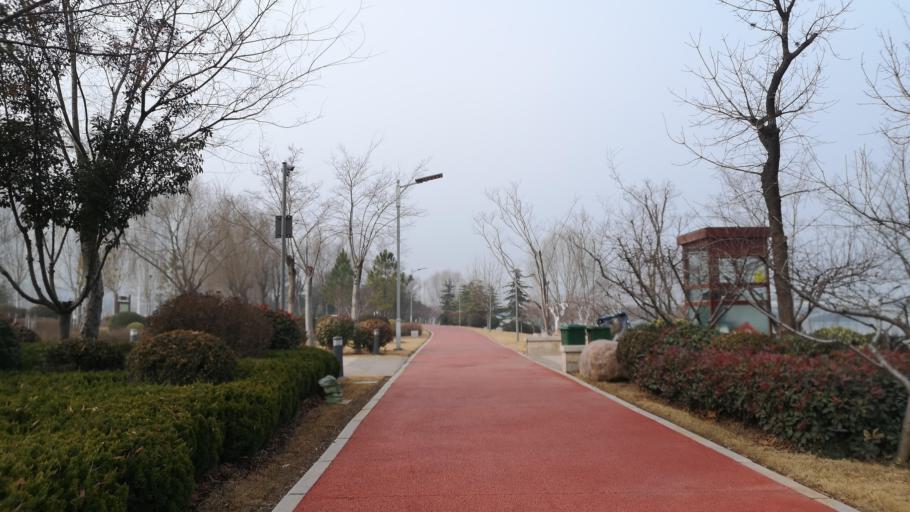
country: CN
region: Henan Sheng
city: Puyang
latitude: 35.8010
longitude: 115.0306
